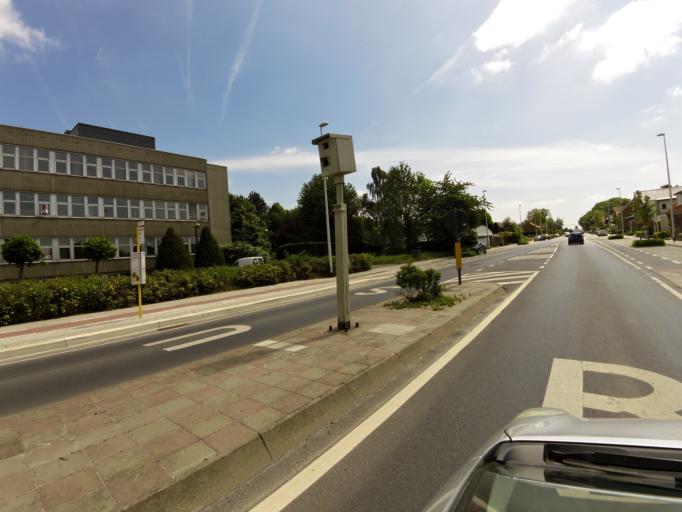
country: BE
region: Flanders
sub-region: Provincie West-Vlaanderen
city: Diksmuide
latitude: 51.0254
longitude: 2.8643
